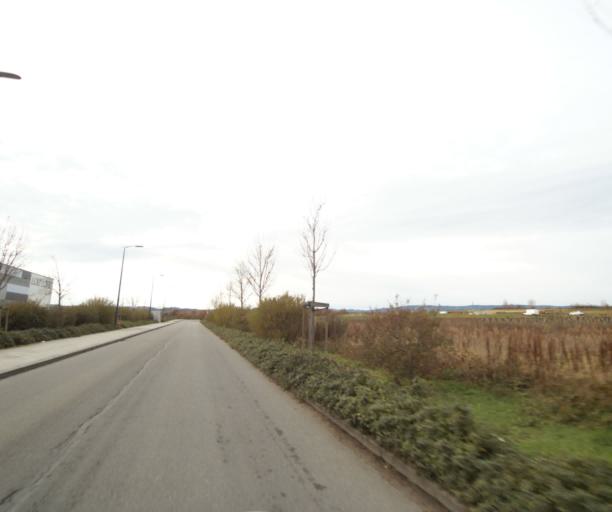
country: FR
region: Rhone-Alpes
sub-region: Departement de la Loire
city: Sury-le-Comtal
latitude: 45.5216
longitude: 4.1943
